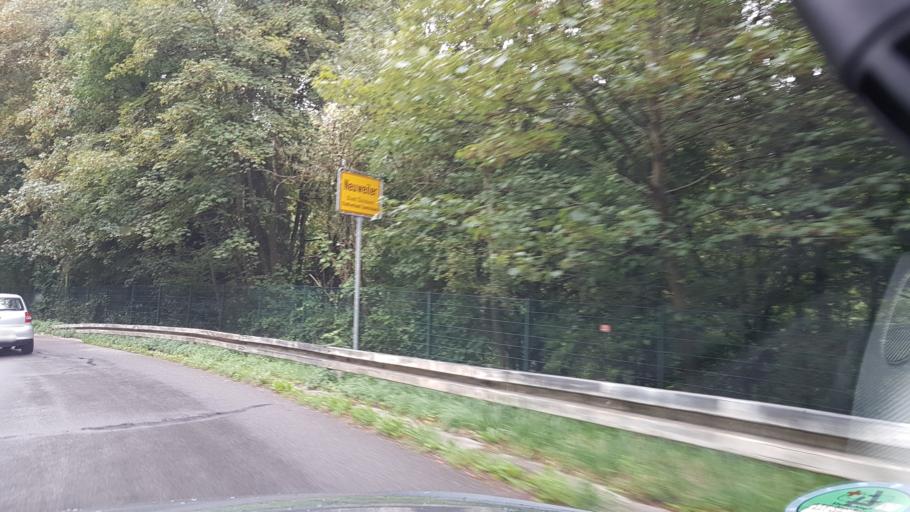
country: DE
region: Saarland
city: Sulzbach
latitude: 49.2902
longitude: 7.0635
